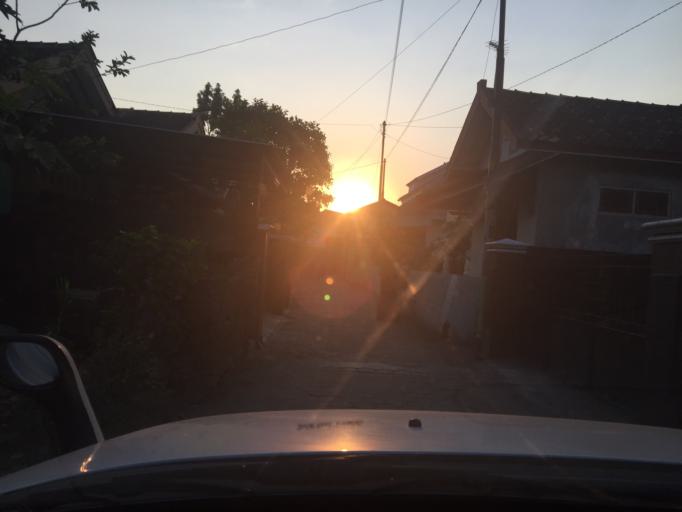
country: ID
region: Daerah Istimewa Yogyakarta
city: Gamping Lor
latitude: -7.7906
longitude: 110.3289
